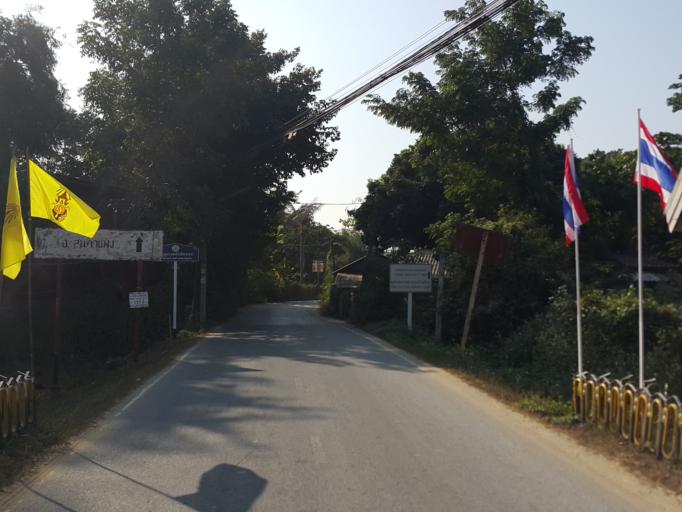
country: TH
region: Chiang Mai
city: San Kamphaeng
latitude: 18.7770
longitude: 99.0821
